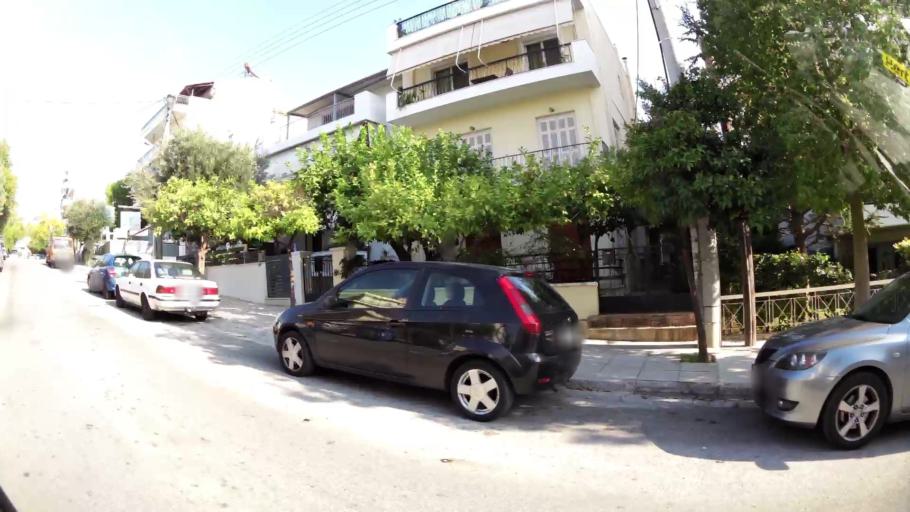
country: GR
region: Attica
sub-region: Nomarchia Athinas
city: Argyroupoli
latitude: 37.9080
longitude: 23.7519
